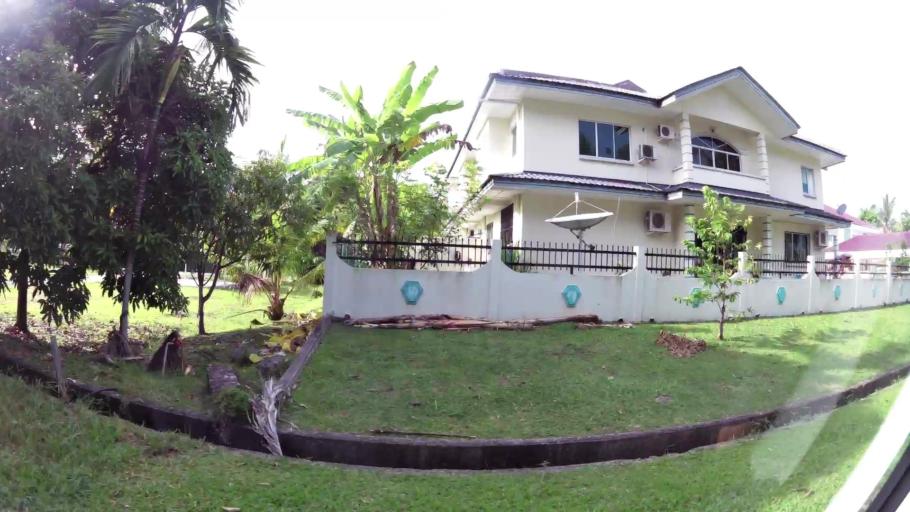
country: BN
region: Brunei and Muara
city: Bandar Seri Begawan
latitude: 4.9098
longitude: 114.8934
